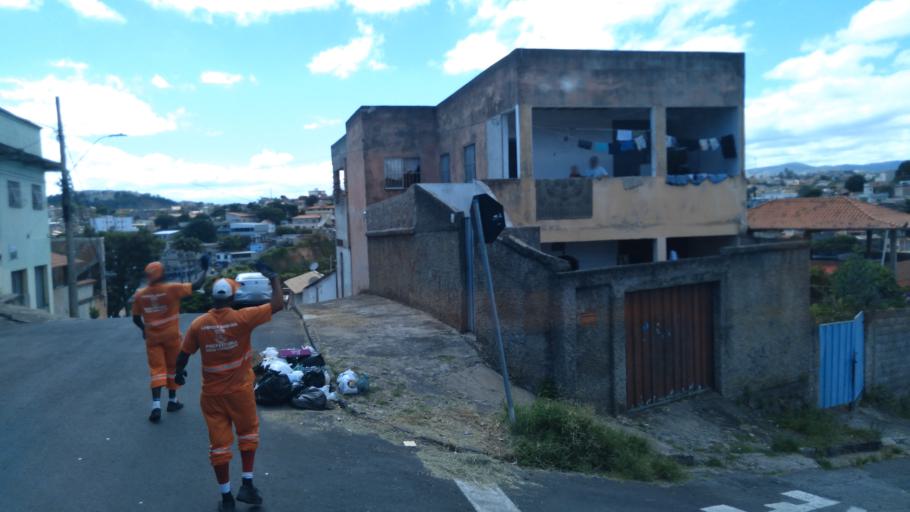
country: BR
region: Minas Gerais
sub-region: Belo Horizonte
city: Belo Horizonte
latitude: -19.8602
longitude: -43.9077
